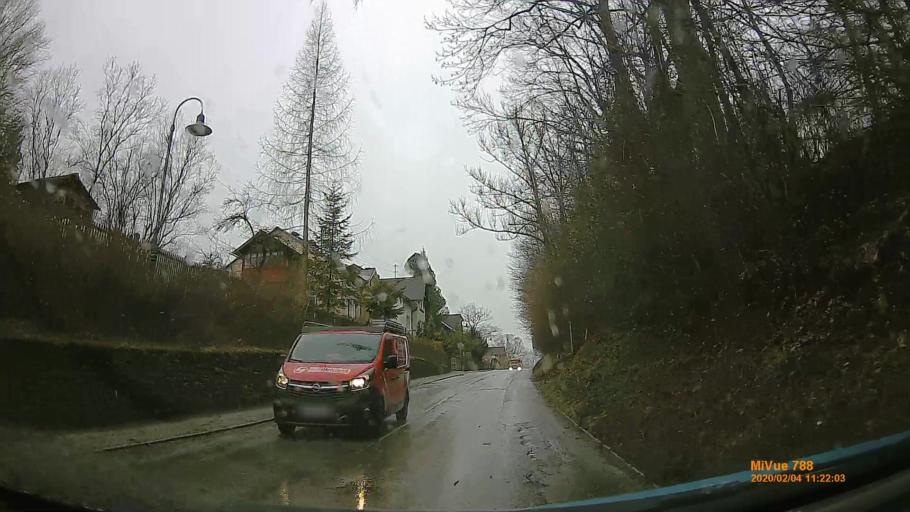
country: AT
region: Styria
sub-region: Politischer Bezirk Bruck-Muerzzuschlag
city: Muerzzuschlag
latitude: 47.6098
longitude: 15.6701
